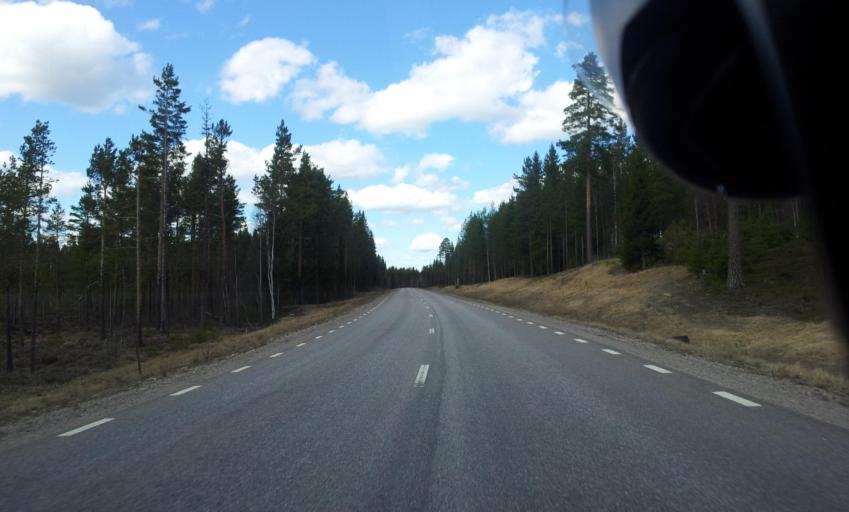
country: SE
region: Gaevleborg
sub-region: Ovanakers Kommun
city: Edsbyn
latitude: 61.1895
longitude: 15.8760
